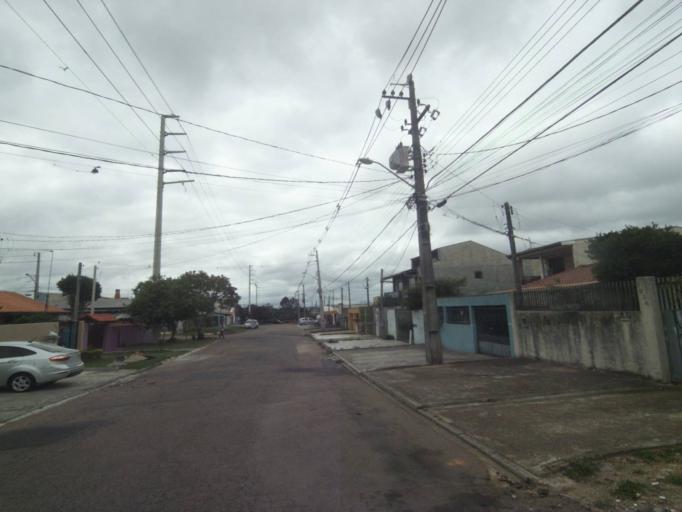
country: BR
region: Parana
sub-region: Sao Jose Dos Pinhais
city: Sao Jose dos Pinhais
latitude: -25.5510
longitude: -49.2600
